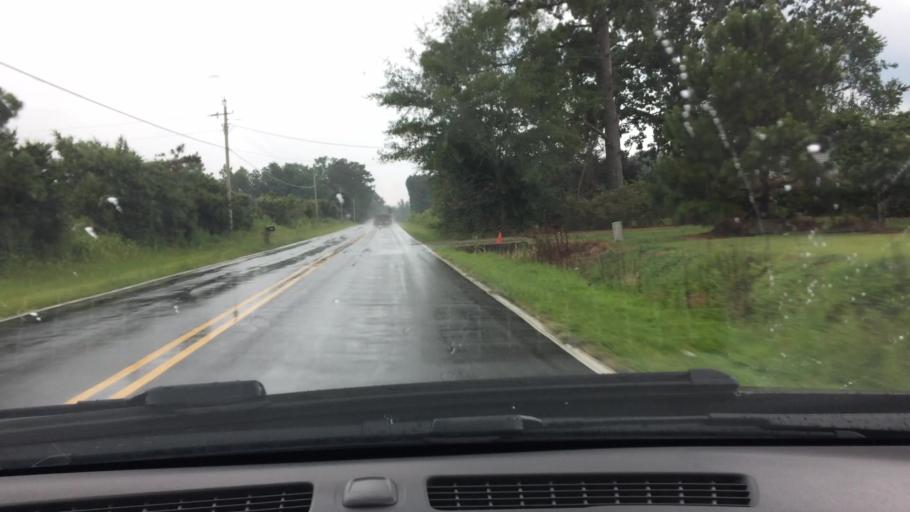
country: US
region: North Carolina
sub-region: Pitt County
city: Winterville
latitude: 35.5175
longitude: -77.3839
